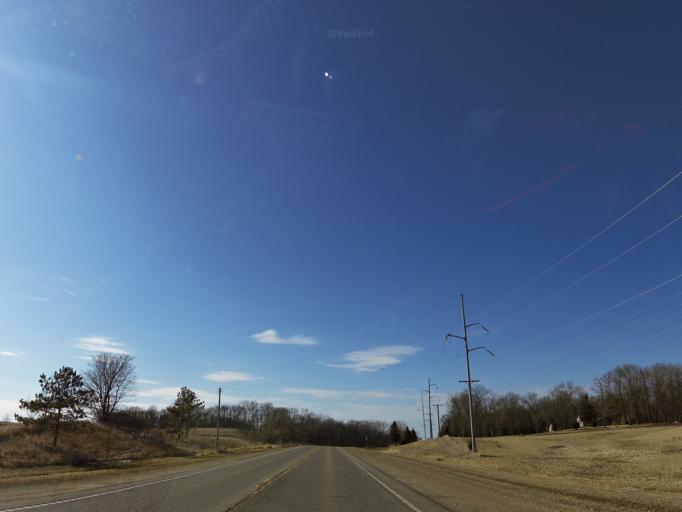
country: US
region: Minnesota
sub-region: Le Sueur County
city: Waterville
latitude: 44.2067
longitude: -93.5504
